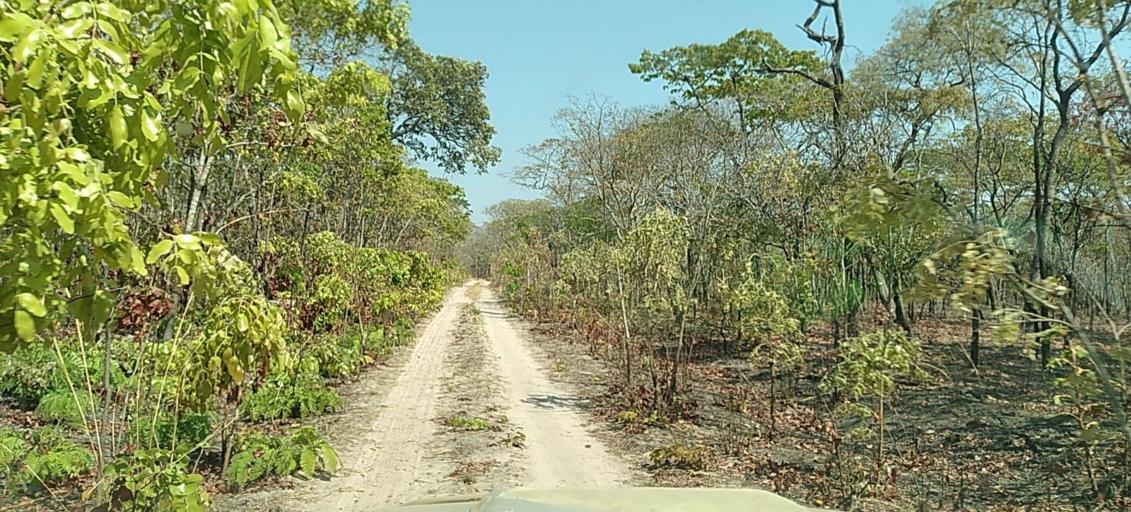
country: ZM
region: North-Western
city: Kalengwa
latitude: -13.3283
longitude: 24.8351
